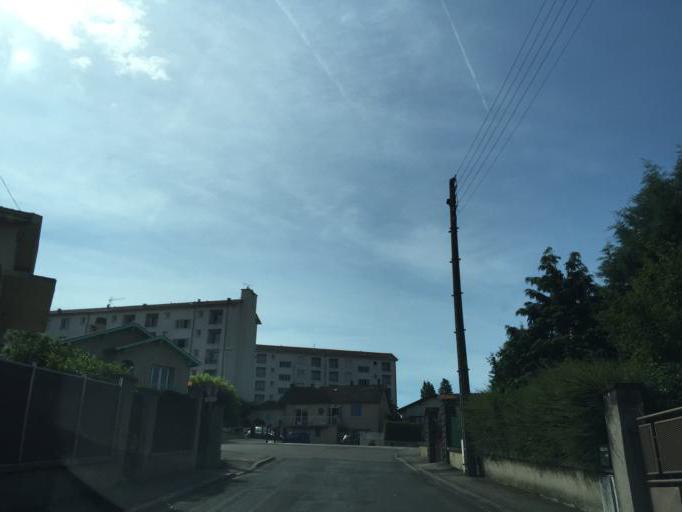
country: FR
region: Rhone-Alpes
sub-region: Departement de la Loire
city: La Grand-Croix
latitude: 45.4847
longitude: 4.5465
